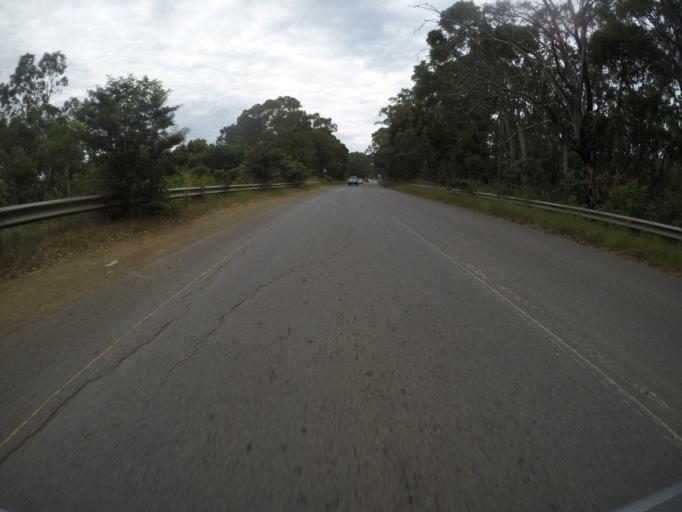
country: ZA
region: Eastern Cape
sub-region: Buffalo City Metropolitan Municipality
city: East London
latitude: -32.9363
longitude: 27.9470
